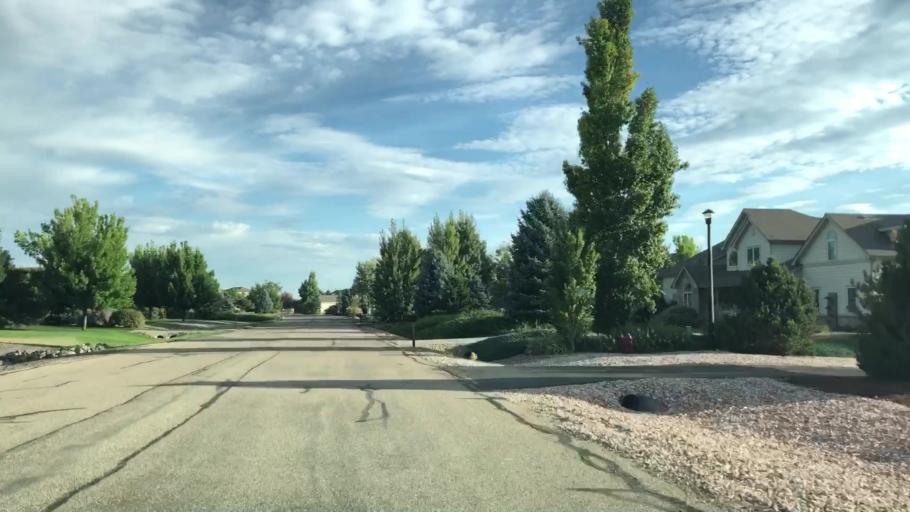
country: US
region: Colorado
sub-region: Weld County
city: Windsor
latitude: 40.4389
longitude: -104.9513
